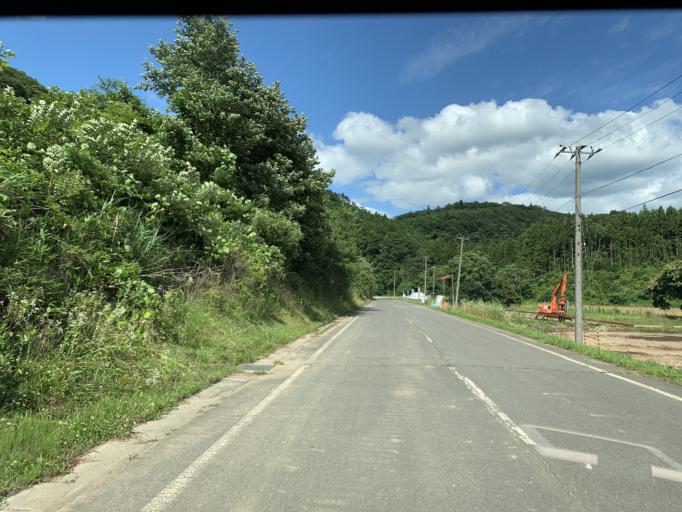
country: JP
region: Iwate
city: Ichinoseki
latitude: 38.9619
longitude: 140.9609
